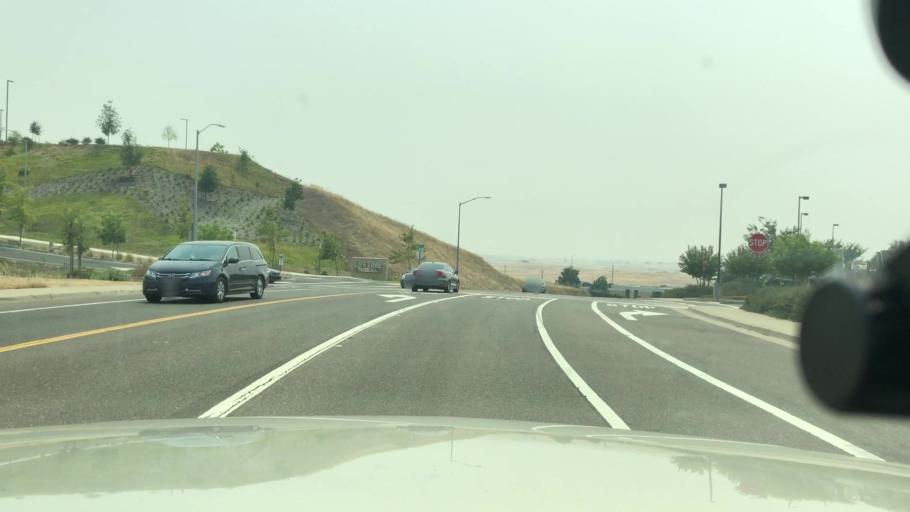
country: US
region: California
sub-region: El Dorado County
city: El Dorado Hills
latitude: 38.6463
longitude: -121.1070
